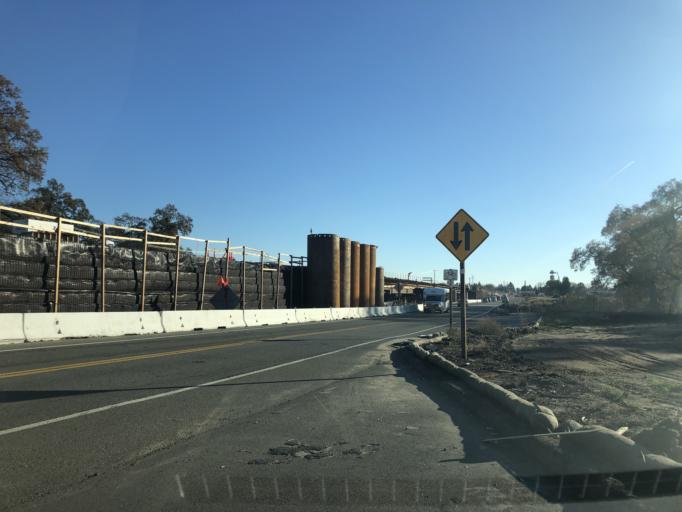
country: US
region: California
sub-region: Sacramento County
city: Antelope
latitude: 38.7379
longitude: -121.3649
